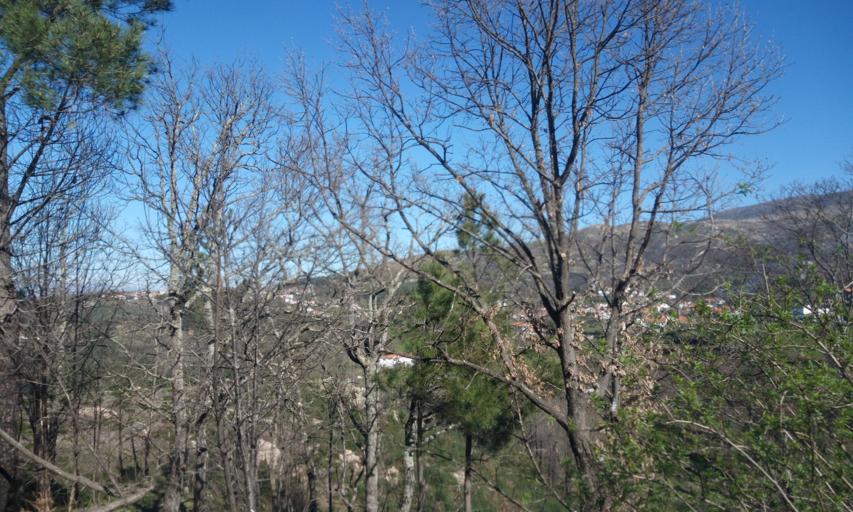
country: PT
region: Guarda
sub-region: Manteigas
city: Manteigas
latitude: 40.4639
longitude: -7.6113
